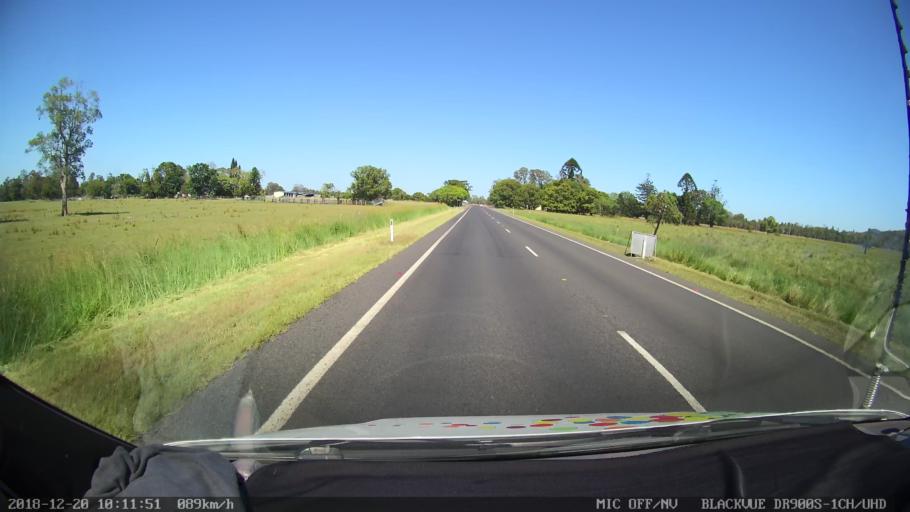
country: AU
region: New South Wales
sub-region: Richmond Valley
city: Casino
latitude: -28.8722
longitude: 153.1525
